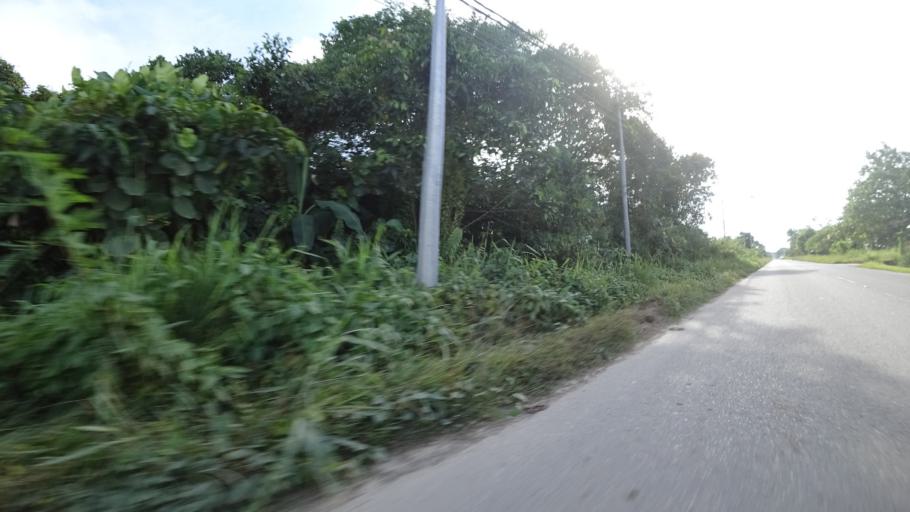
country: BN
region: Brunei and Muara
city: Bandar Seri Begawan
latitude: 4.8442
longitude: 114.8533
